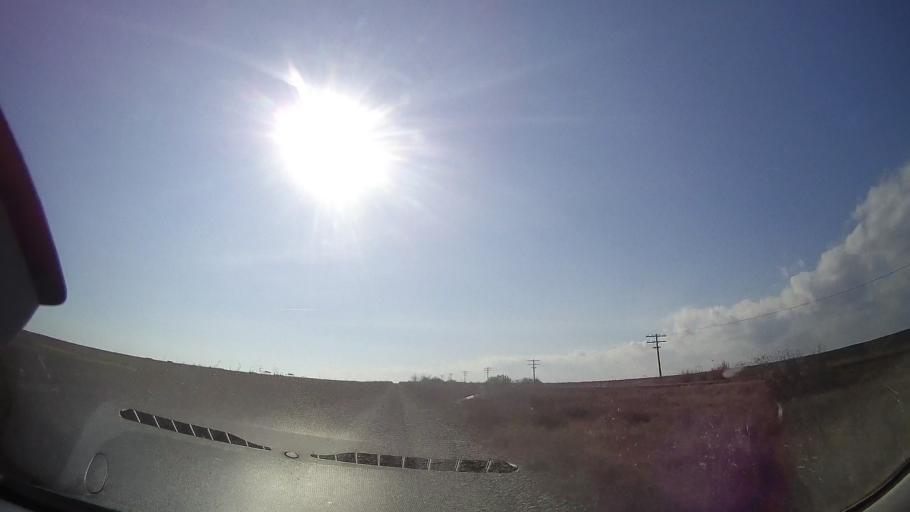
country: RO
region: Constanta
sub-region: Comuna Costinesti
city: Schitu
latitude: 43.9210
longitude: 28.6305
